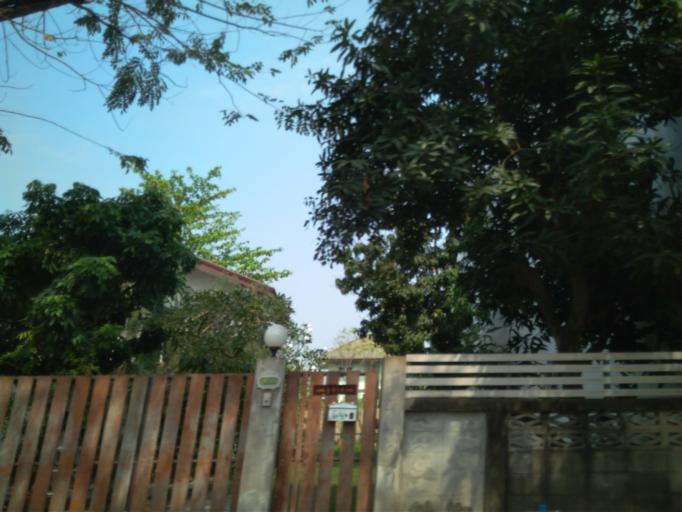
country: TH
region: Bangkok
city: Taling Chan
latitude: 13.7784
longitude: 100.4500
